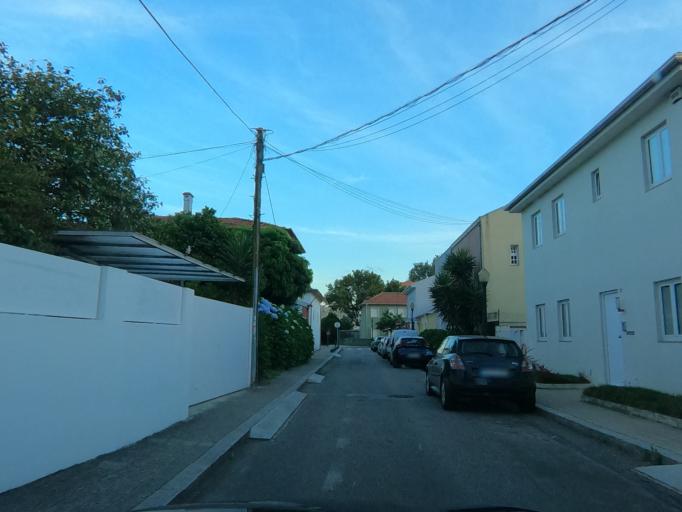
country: PT
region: Porto
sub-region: Porto
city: Porto
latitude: 41.1756
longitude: -8.6198
